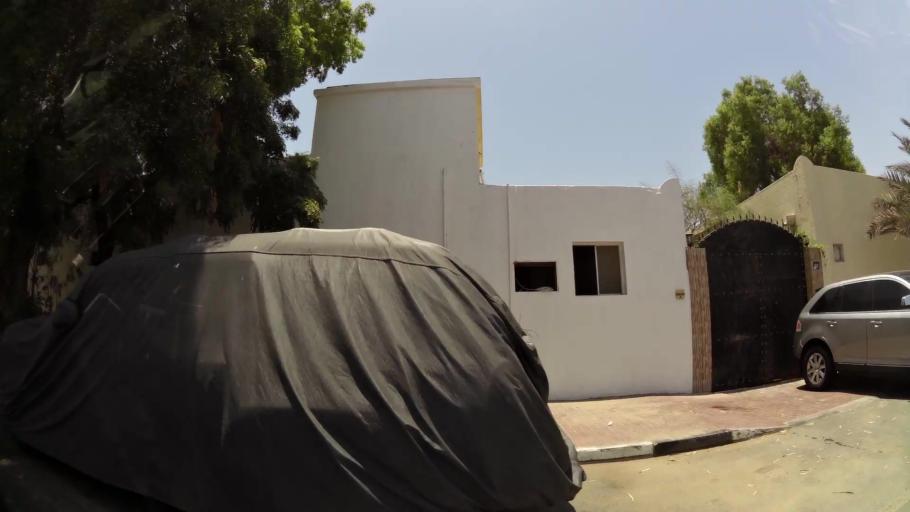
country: AE
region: Ash Shariqah
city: Sharjah
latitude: 25.2280
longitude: 55.2662
